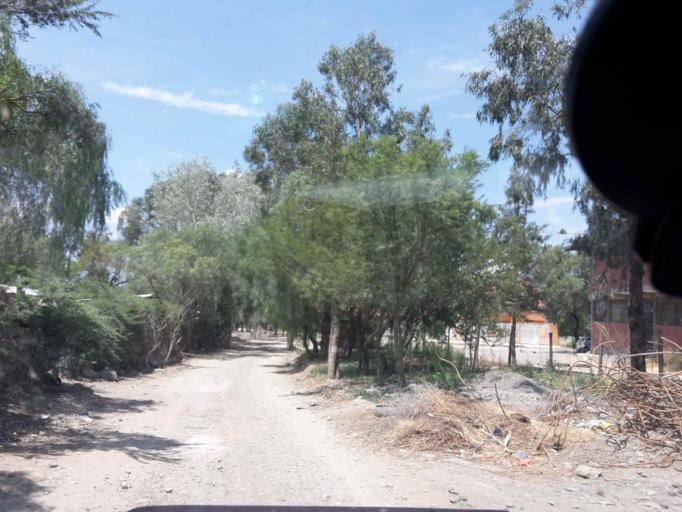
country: BO
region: Cochabamba
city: Cochabamba
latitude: -17.3358
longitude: -66.2139
